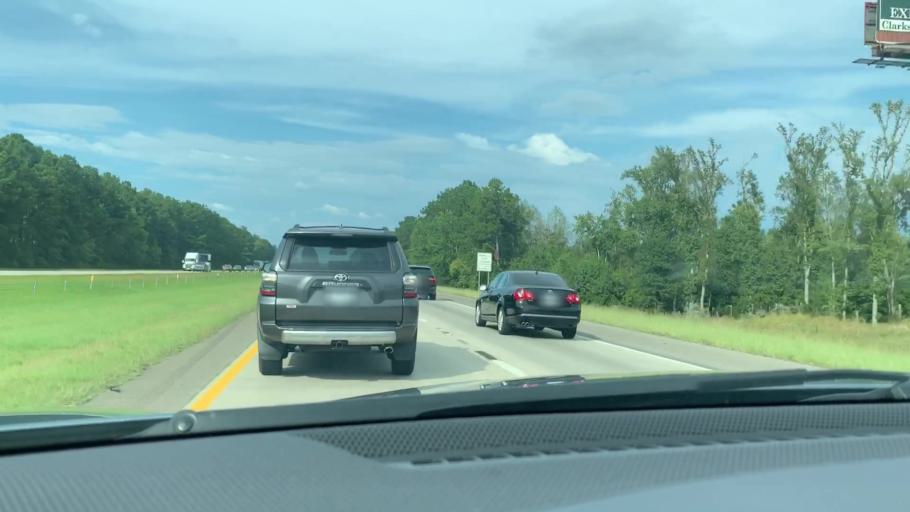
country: US
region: South Carolina
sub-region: Colleton County
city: Walterboro
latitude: 32.9460
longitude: -80.6834
